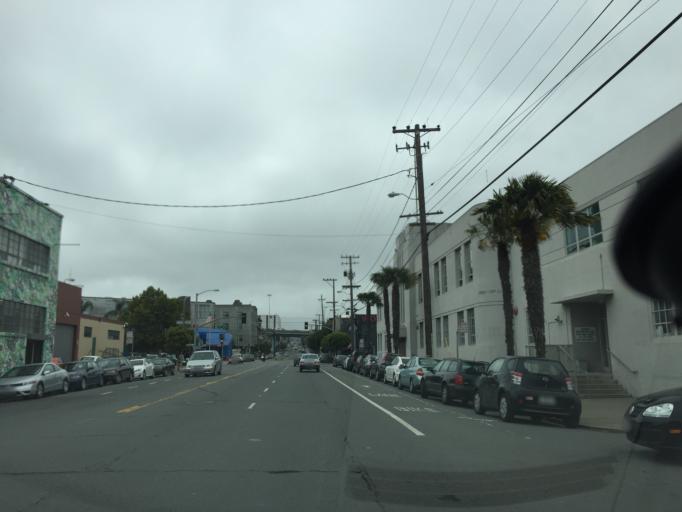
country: US
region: California
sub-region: San Francisco County
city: San Francisco
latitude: 37.7663
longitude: -122.4007
